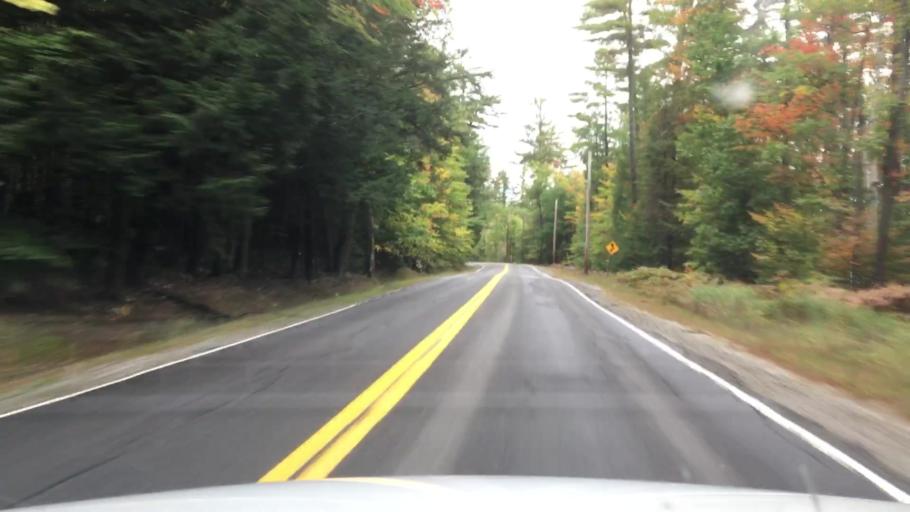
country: US
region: Maine
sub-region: Oxford County
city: Bethel
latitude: 44.3587
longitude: -70.7936
